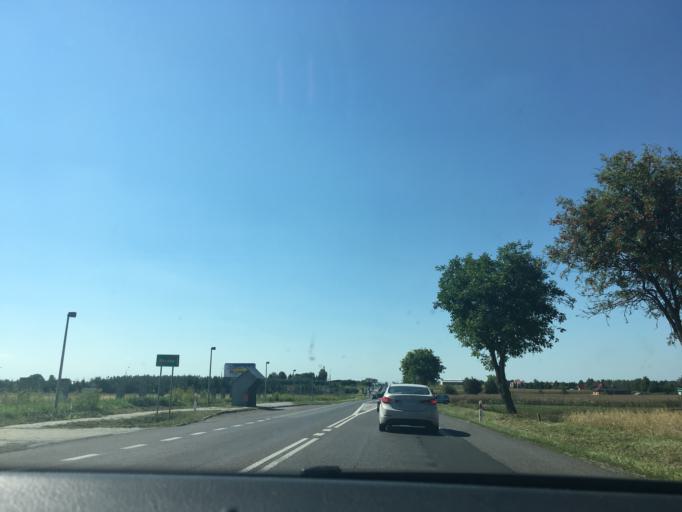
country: PL
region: Lublin Voivodeship
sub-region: Powiat lubelski
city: Niemce
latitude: 51.3453
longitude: 22.6192
